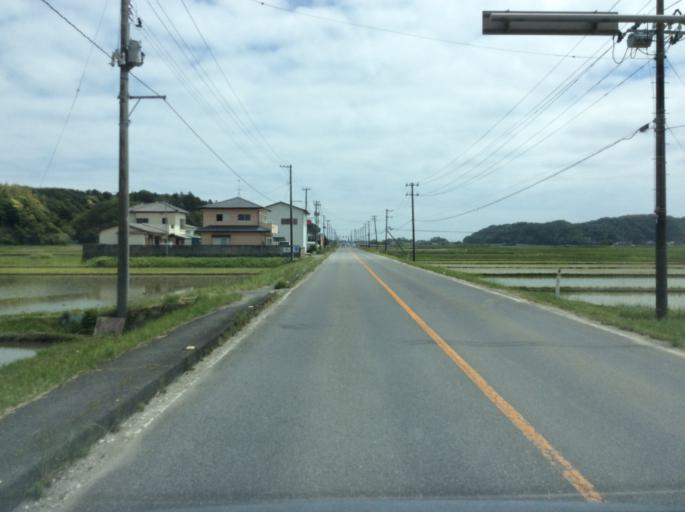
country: JP
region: Fukushima
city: Iwaki
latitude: 37.0314
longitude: 140.9371
